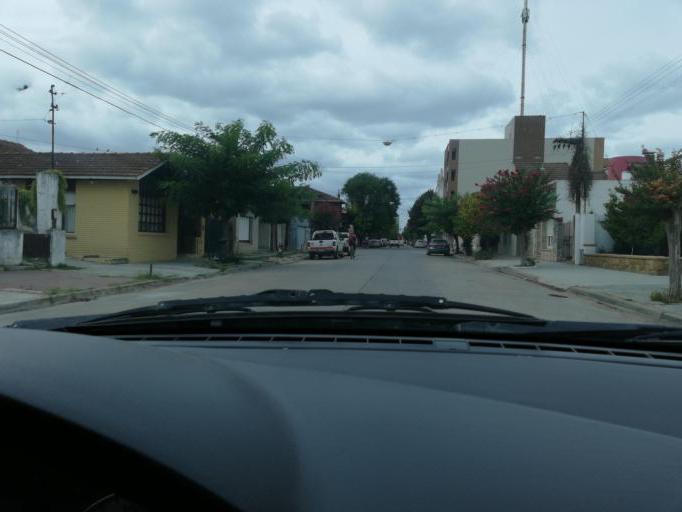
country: AR
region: Buenos Aires
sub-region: Partido de Balcarce
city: Balcarce
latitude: -37.8468
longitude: -58.2610
